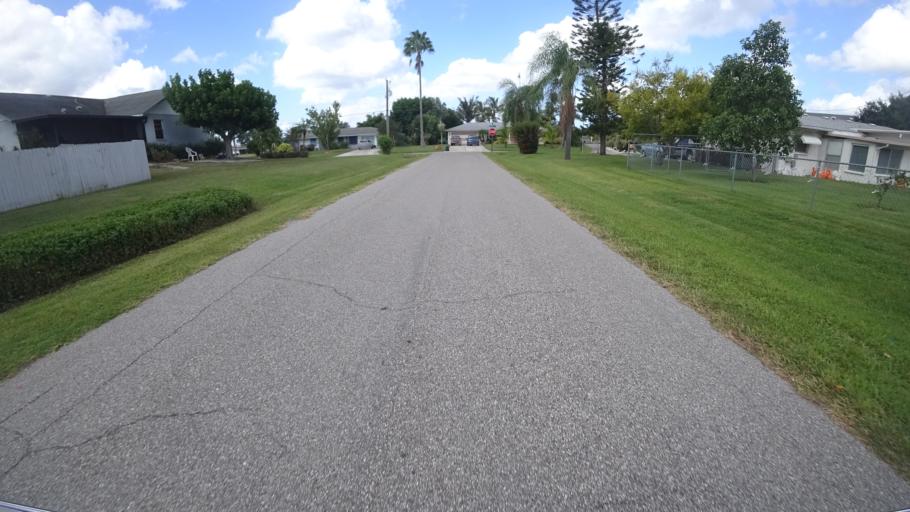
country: US
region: Florida
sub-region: Manatee County
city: Memphis
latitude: 27.5597
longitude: -82.5684
